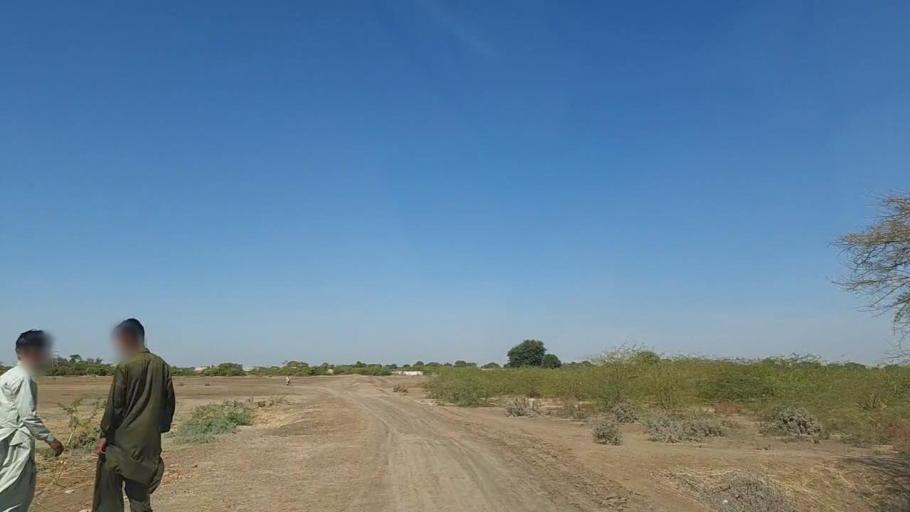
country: PK
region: Sindh
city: Samaro
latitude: 25.3118
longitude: 69.5148
